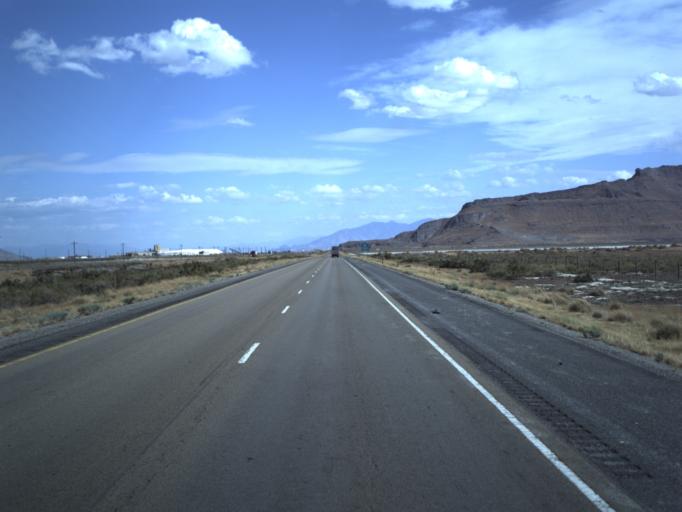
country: US
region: Utah
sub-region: Tooele County
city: Grantsville
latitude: 40.7492
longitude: -112.6886
